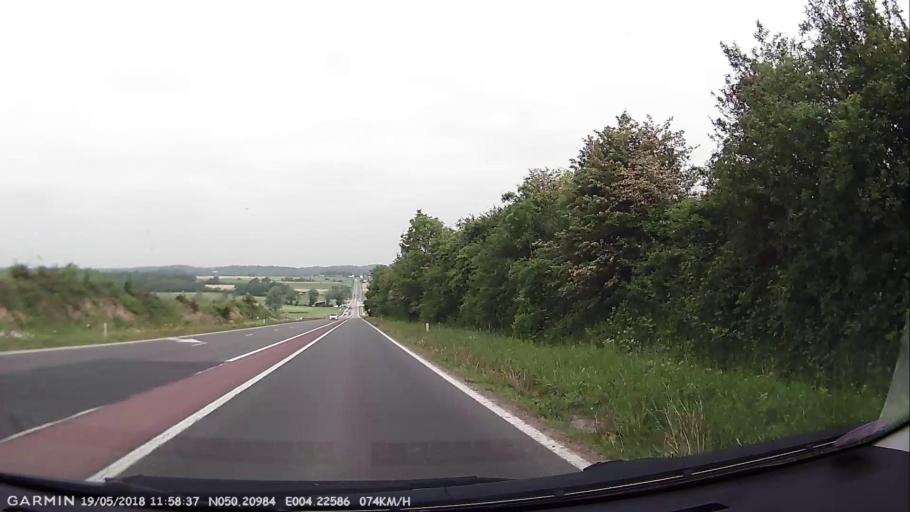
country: BE
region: Wallonia
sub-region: Province du Hainaut
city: Beaumont
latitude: 50.2101
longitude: 4.2259
